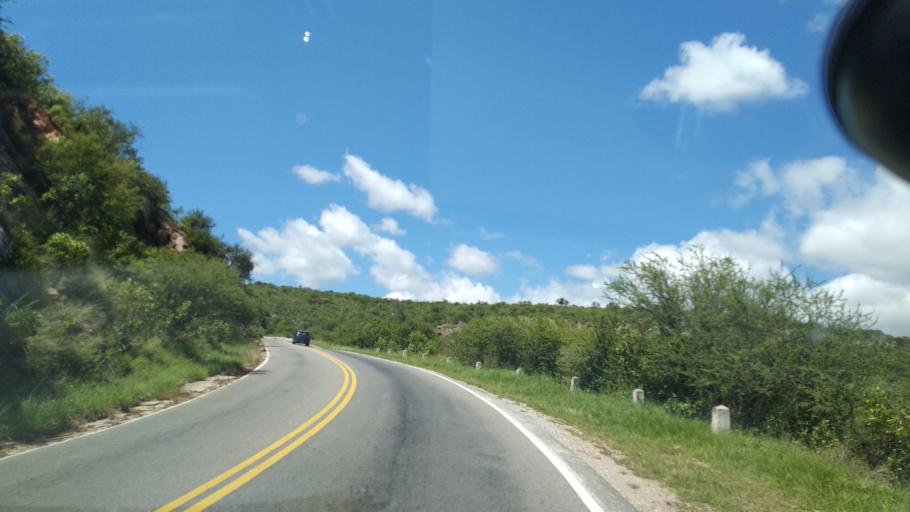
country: AR
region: Cordoba
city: Villa Cura Brochero
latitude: -31.6975
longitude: -65.0524
